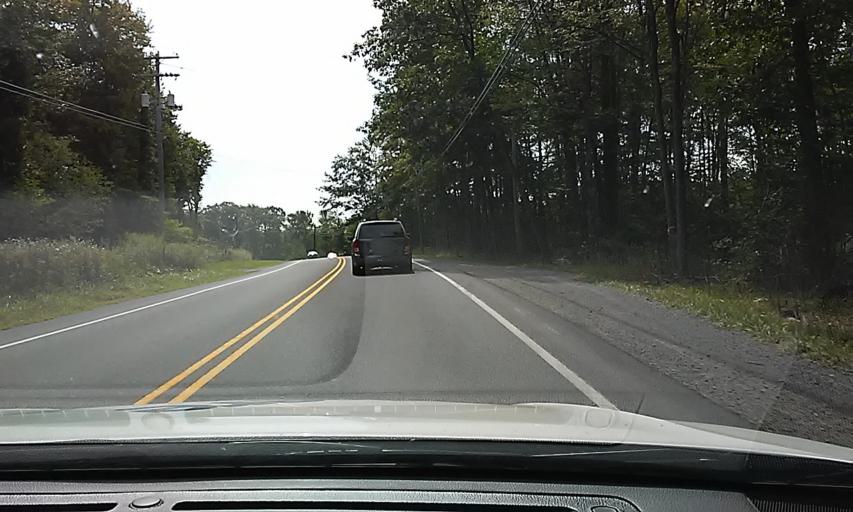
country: US
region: Pennsylvania
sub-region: Elk County
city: Saint Marys
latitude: 41.3610
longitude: -78.5528
